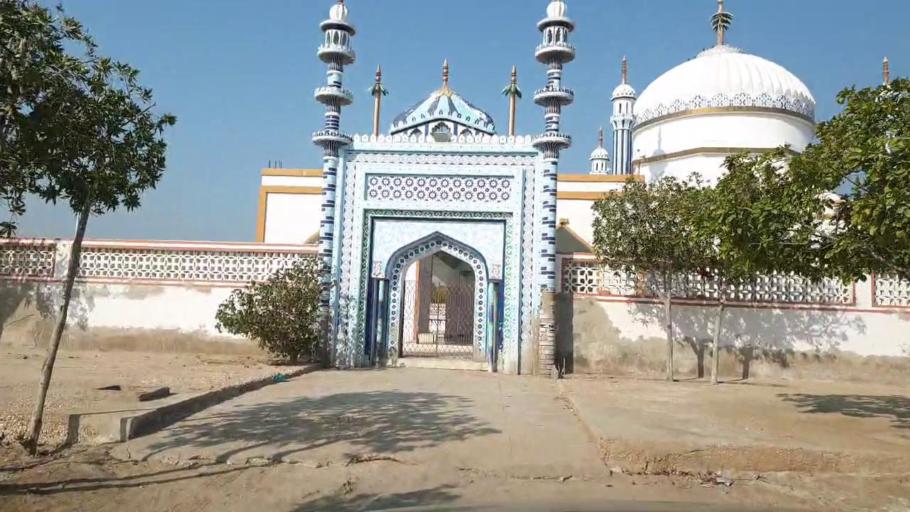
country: PK
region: Sindh
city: Tando Allahyar
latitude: 25.5112
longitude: 68.7247
